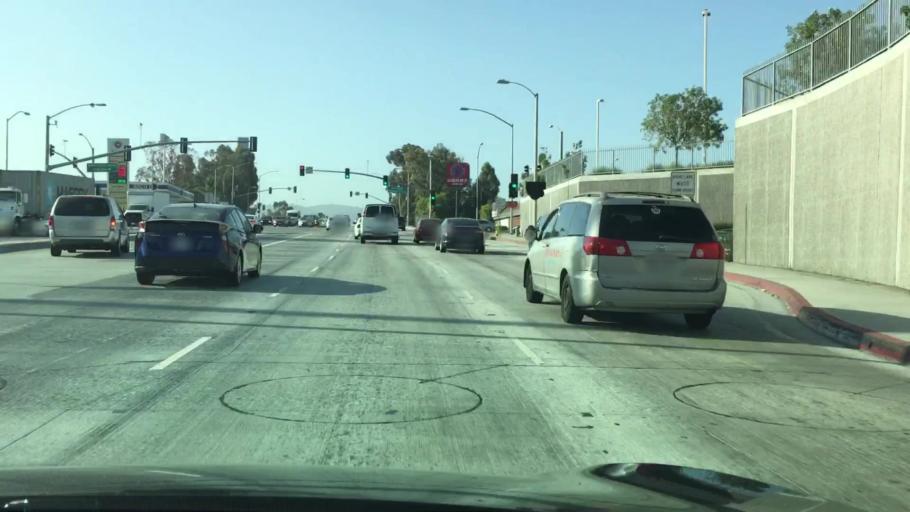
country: US
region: California
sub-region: Los Angeles County
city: South San Jose Hills
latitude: 33.9971
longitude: -117.8885
